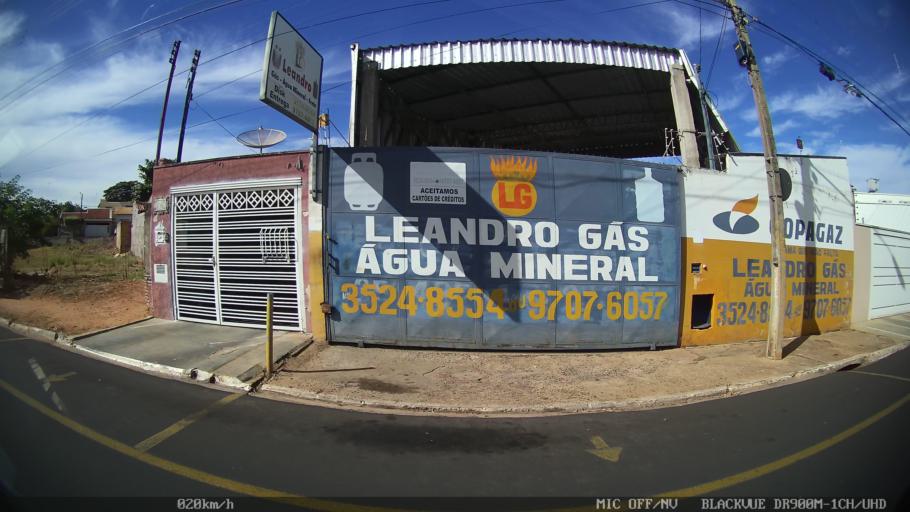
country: BR
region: Sao Paulo
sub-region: Catanduva
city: Catanduva
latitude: -21.1294
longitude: -48.9636
